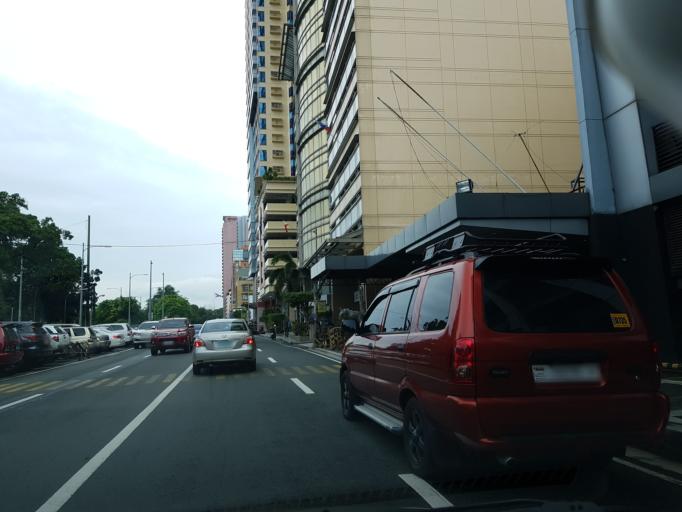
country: PH
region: Metro Manila
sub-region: City of Manila
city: Port Area
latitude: 14.5758
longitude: 120.9799
